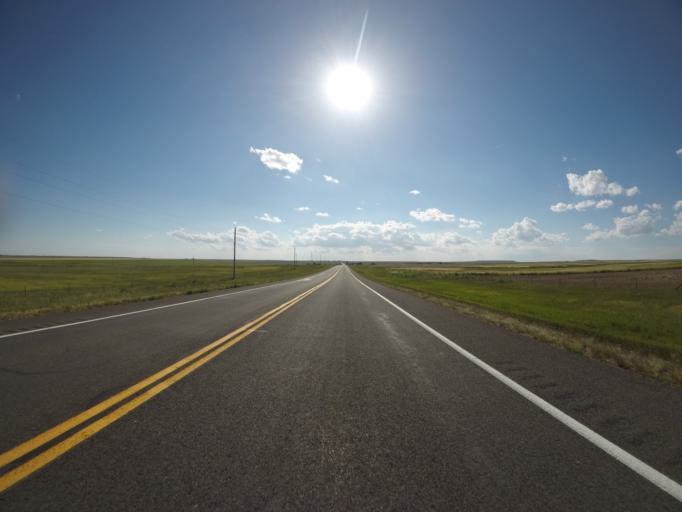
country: US
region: Colorado
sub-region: Morgan County
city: Fort Morgan
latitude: 40.6111
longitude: -103.7795
